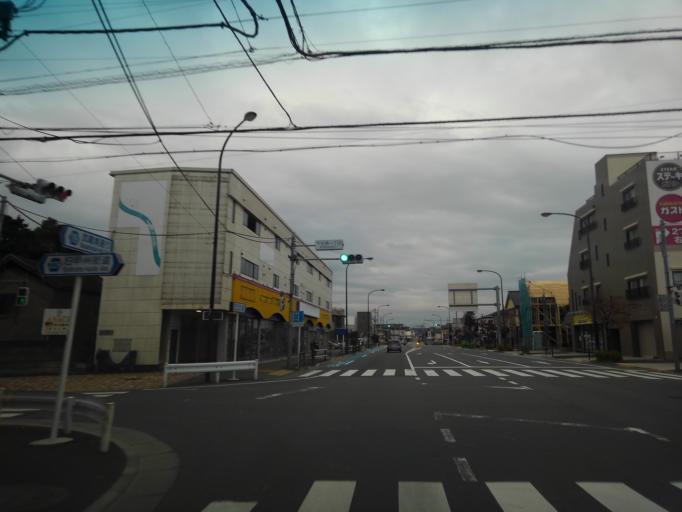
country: JP
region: Tokyo
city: Chofugaoka
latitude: 35.6548
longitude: 139.5389
